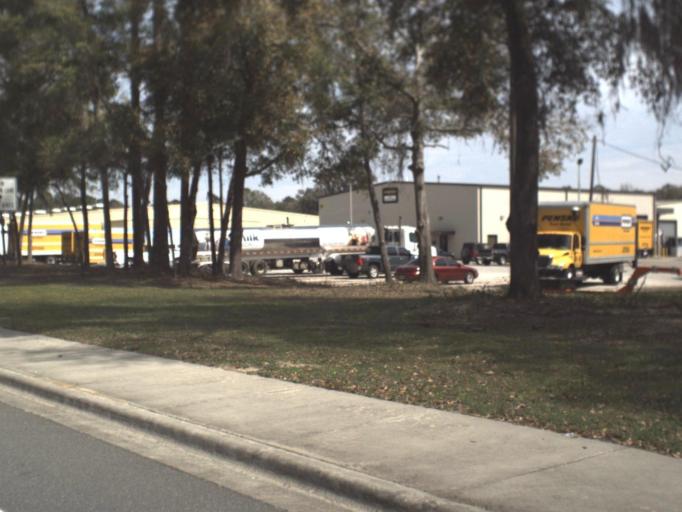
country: US
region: Florida
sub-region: Gadsden County
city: Midway
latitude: 30.5172
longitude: -84.3662
